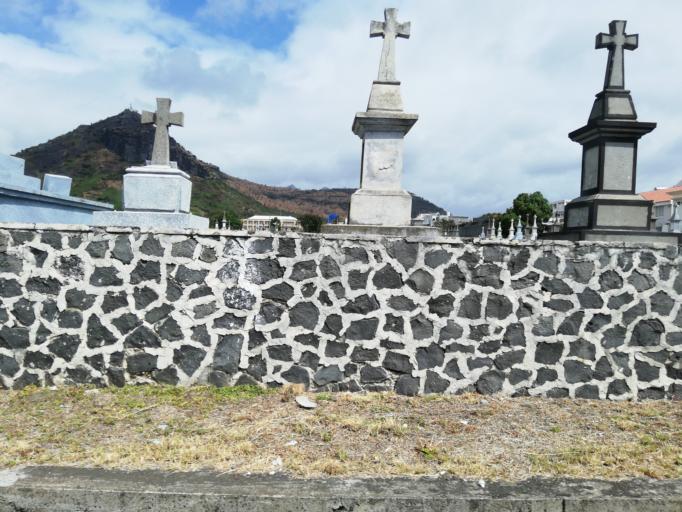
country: MU
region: Port Louis
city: Port Louis
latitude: -20.1615
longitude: 57.4846
